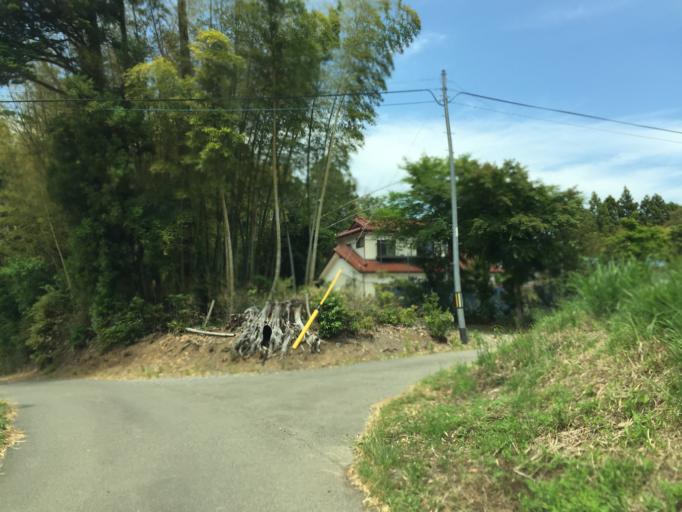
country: JP
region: Miyagi
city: Marumori
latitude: 37.7710
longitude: 140.8967
